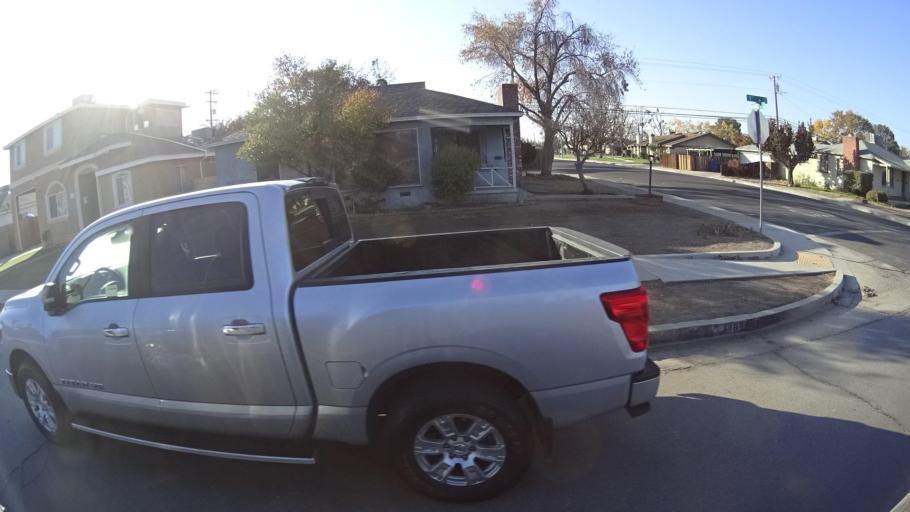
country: US
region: California
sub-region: Kern County
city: Delano
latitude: 35.7686
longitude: -119.2386
